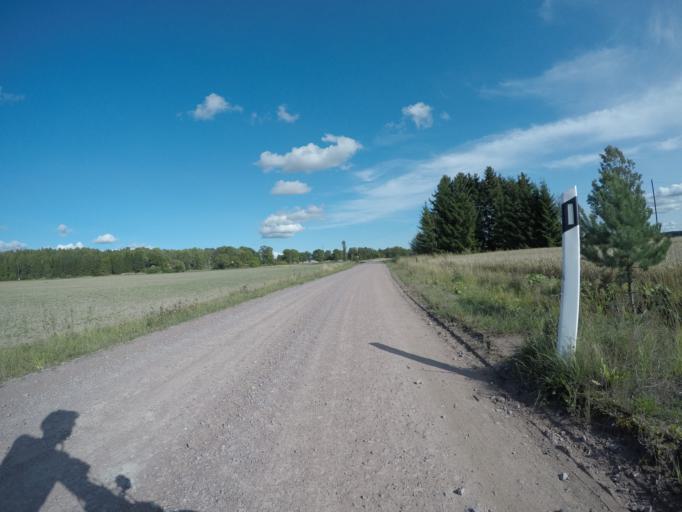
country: SE
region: Soedermanland
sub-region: Eskilstuna Kommun
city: Kvicksund
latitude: 59.5118
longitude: 16.3462
